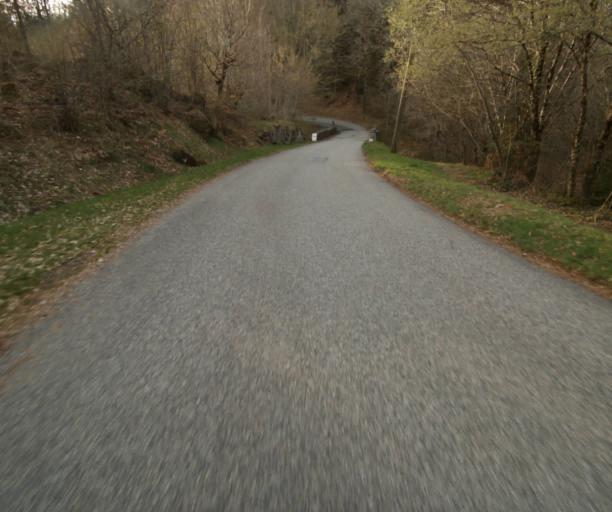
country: FR
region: Limousin
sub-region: Departement de la Correze
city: Argentat
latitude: 45.2200
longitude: 1.9746
